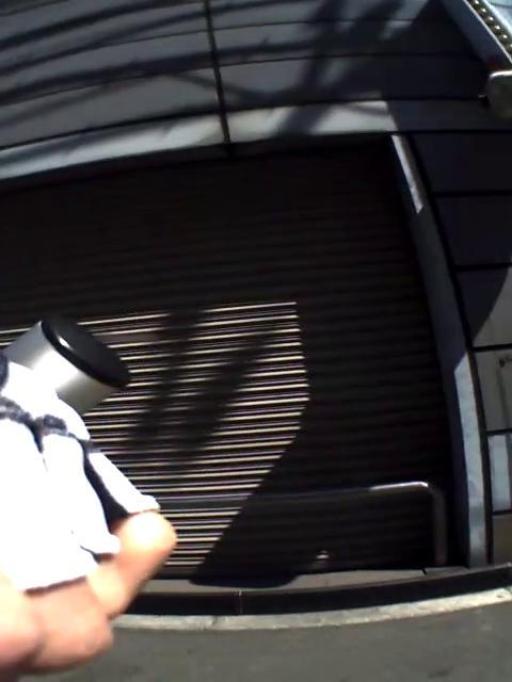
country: JP
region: Osaka
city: Osaka-shi
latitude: 34.6564
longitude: 135.5051
